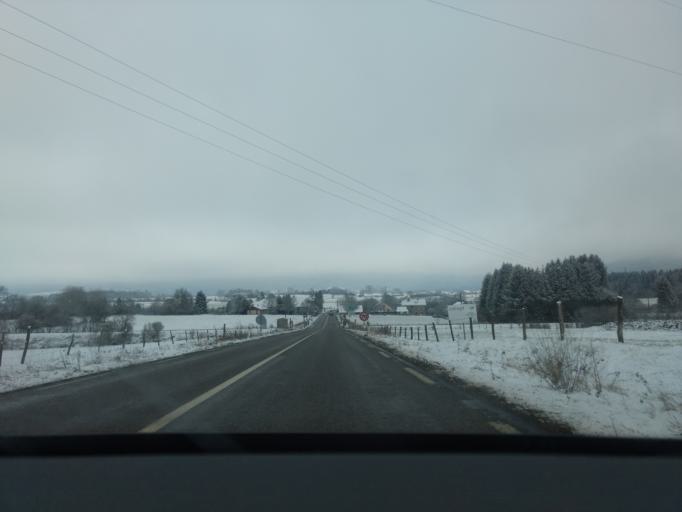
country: FR
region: Franche-Comte
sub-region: Departement du Jura
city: Champagnole
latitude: 46.7802
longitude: 5.8910
